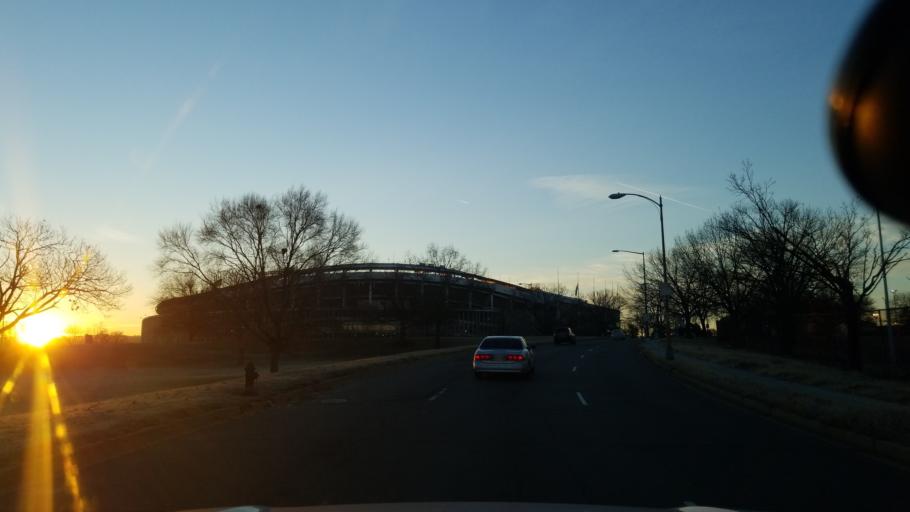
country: US
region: Maryland
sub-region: Prince George's County
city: Colmar Manor
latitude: 38.8926
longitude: -76.9743
